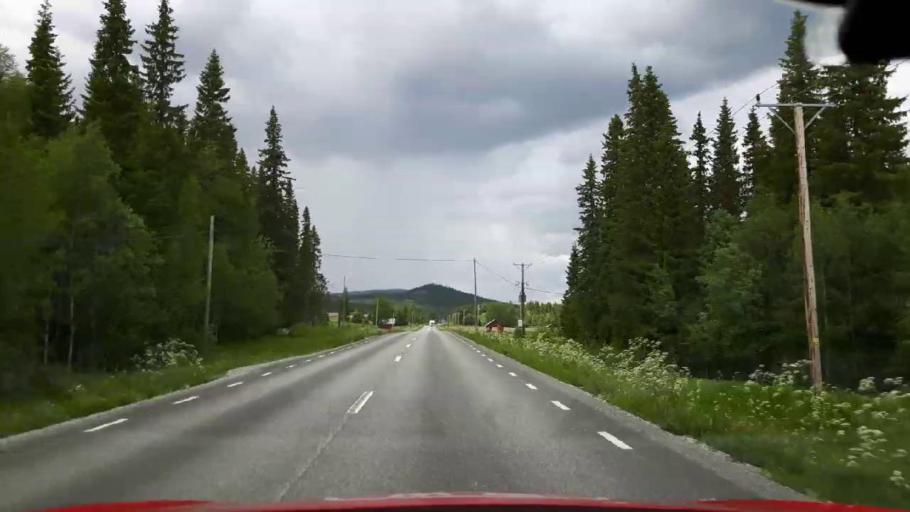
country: SE
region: Jaemtland
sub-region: Krokoms Kommun
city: Krokom
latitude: 63.6783
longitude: 14.3376
